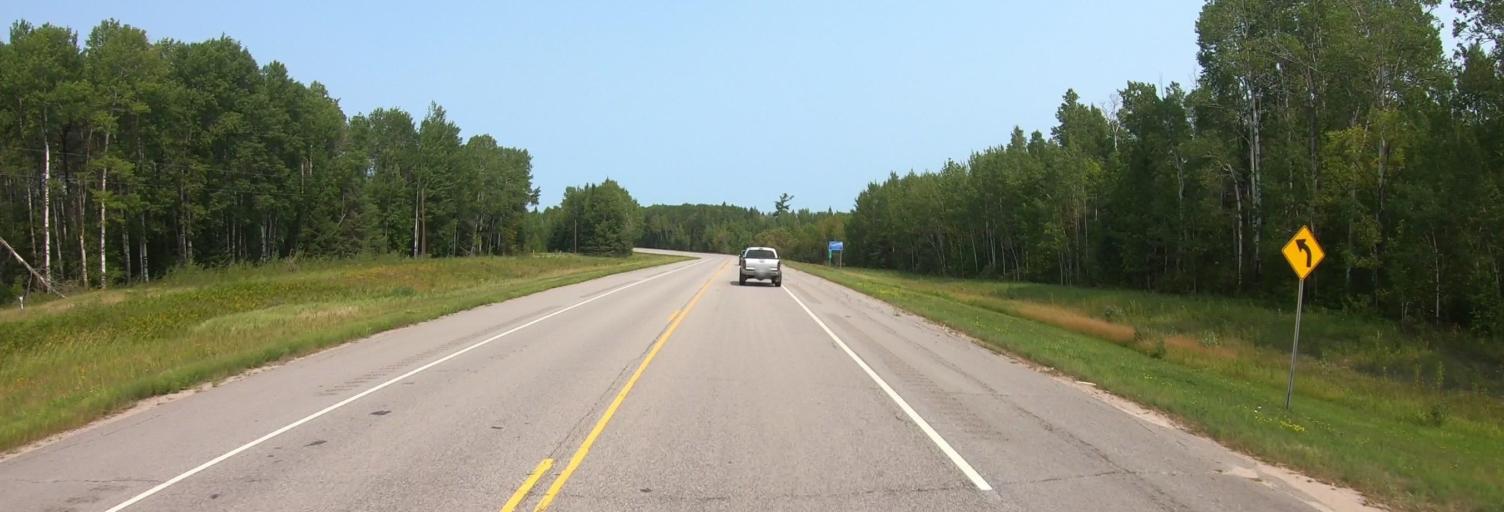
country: CA
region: Ontario
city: Fort Frances
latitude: 48.3616
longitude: -92.9632
